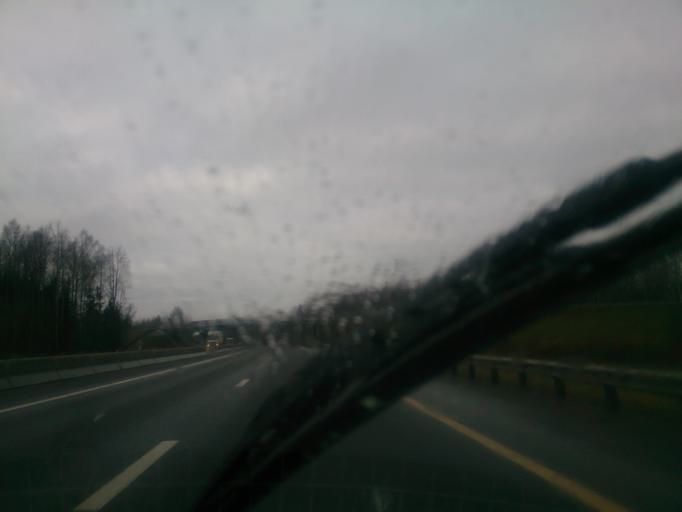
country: RU
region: Leningrad
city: Ul'yanovka
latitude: 59.5918
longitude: 30.7799
